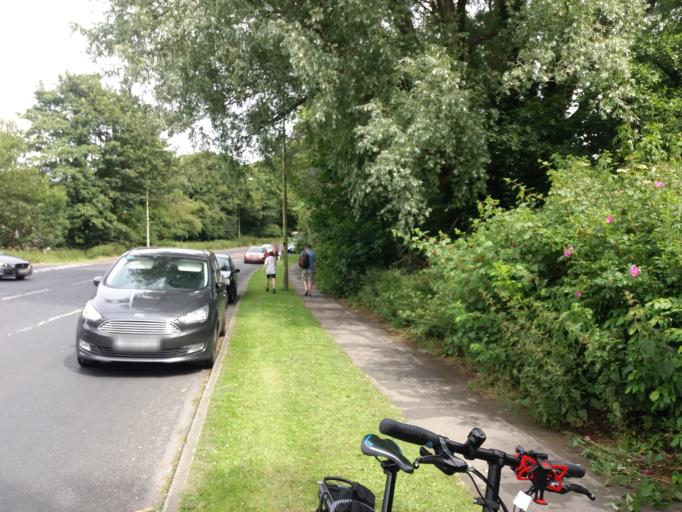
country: GB
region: England
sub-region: Lancashire
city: Clayton-le-Woods
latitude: 53.7070
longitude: -2.6355
